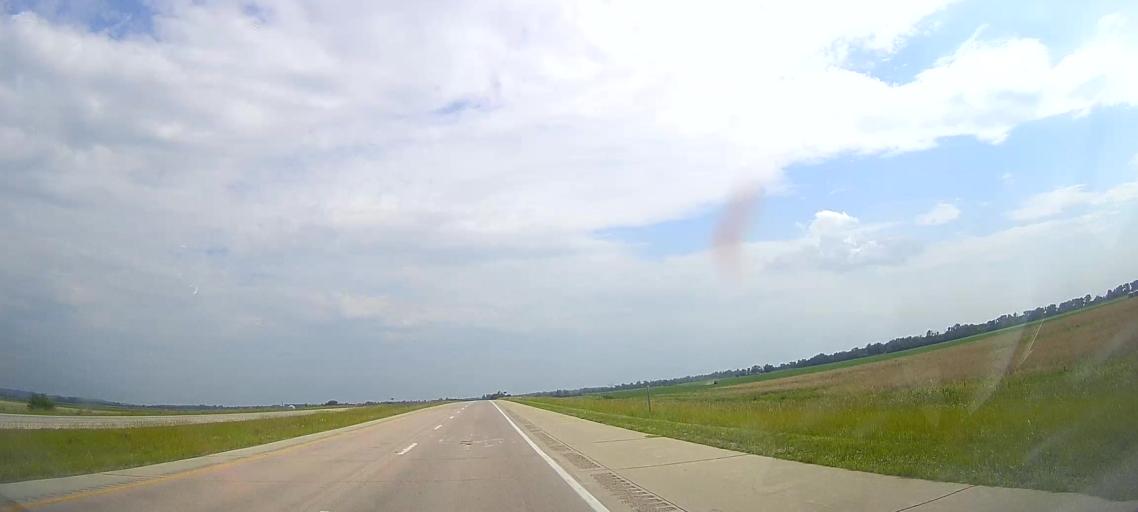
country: US
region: Nebraska
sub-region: Burt County
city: Tekamah
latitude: 41.8678
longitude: -96.1035
